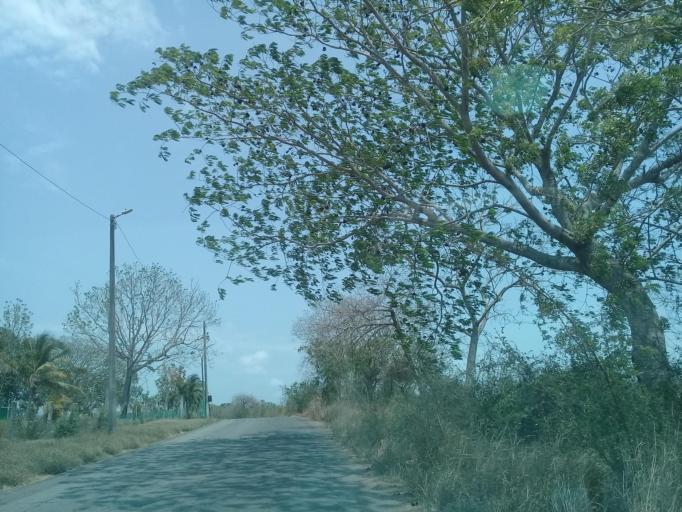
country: MX
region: Veracruz
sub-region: Veracruz
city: Delfino Victoria (Santa Fe)
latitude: 19.1701
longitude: -96.2907
